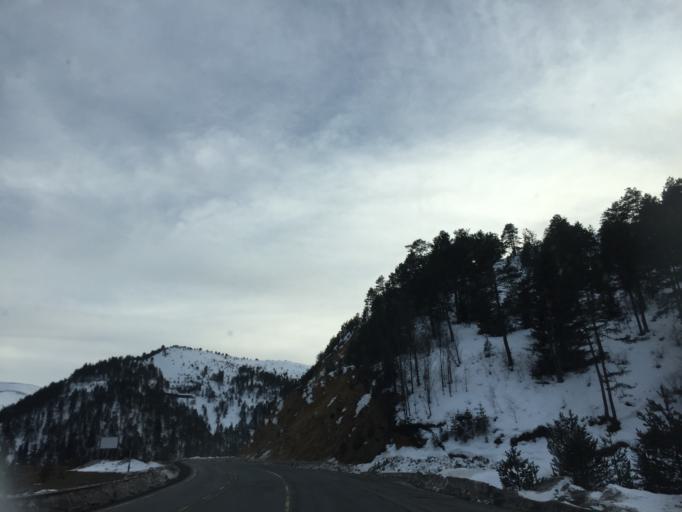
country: TR
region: Gumushane
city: Yaglidere
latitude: 40.6619
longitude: 39.4145
